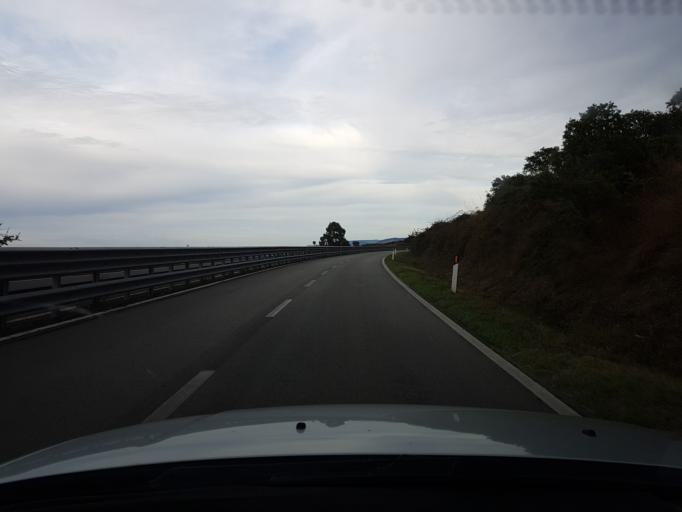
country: IT
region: Sardinia
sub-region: Provincia di Oristano
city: Sedilo
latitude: 40.1800
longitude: 8.9437
